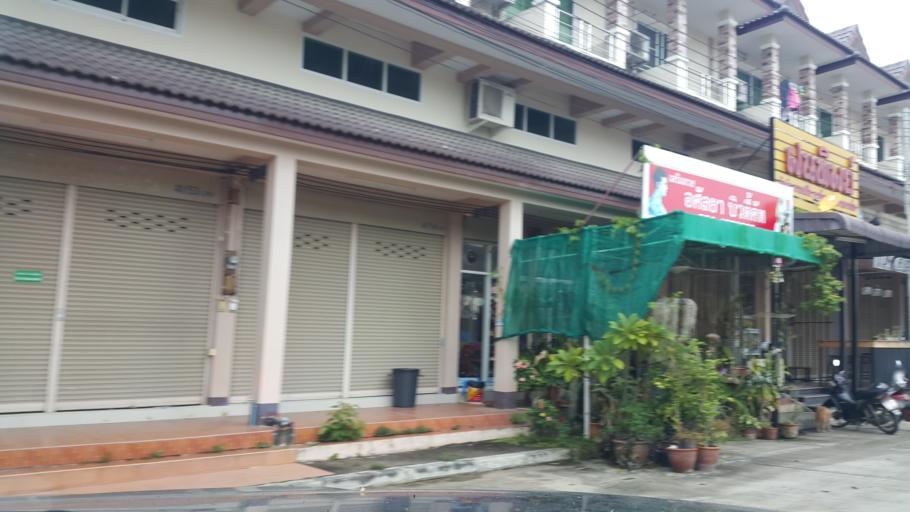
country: TH
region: Chiang Mai
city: San Kamphaeng
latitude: 18.7730
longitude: 99.0860
